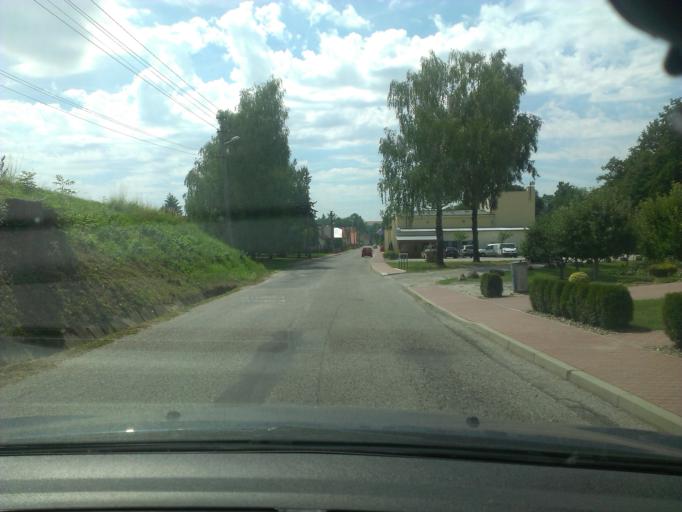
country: SK
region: Trenciansky
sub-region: Okres Myjava
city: Myjava
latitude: 48.7897
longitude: 17.5876
